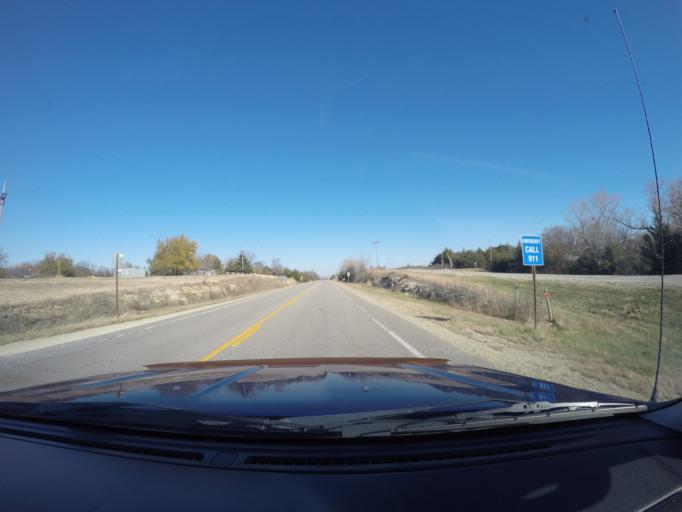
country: US
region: Kansas
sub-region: Marshall County
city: Blue Rapids
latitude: 39.4136
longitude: -96.7644
